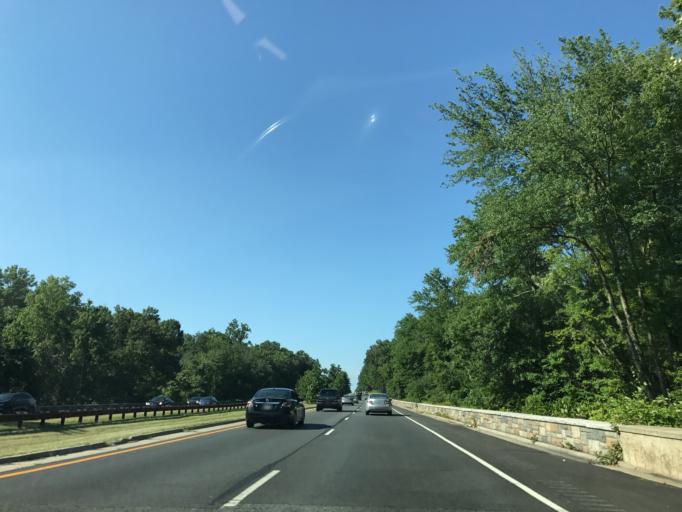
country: US
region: Maryland
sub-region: Prince George's County
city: Greenbelt
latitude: 39.0203
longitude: -76.8584
